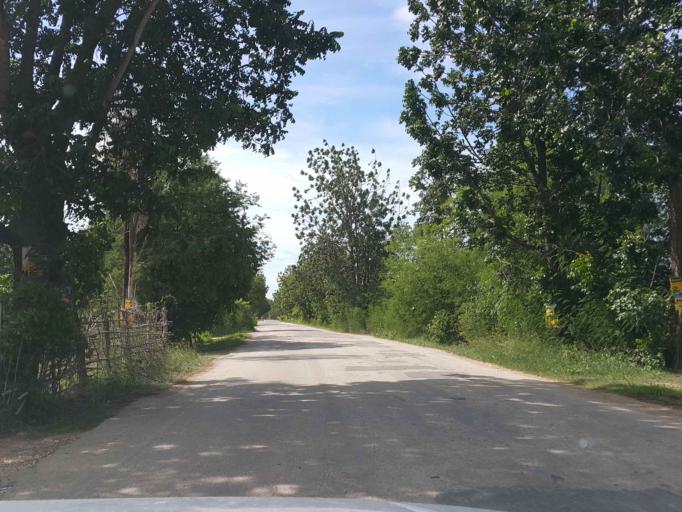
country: TH
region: Sukhothai
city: Ban Dan Lan Hoi
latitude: 17.1415
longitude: 99.5235
